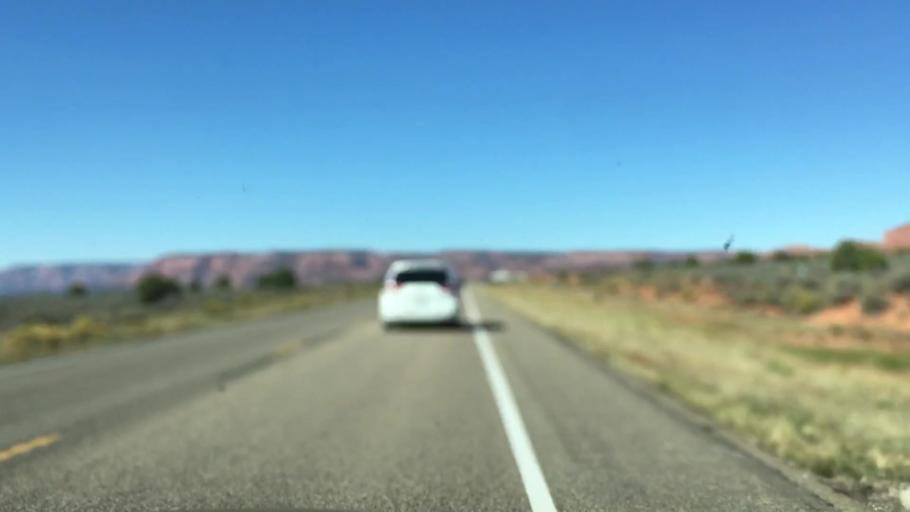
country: US
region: Utah
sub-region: Kane County
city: Kanab
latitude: 37.0259
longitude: -112.4680
